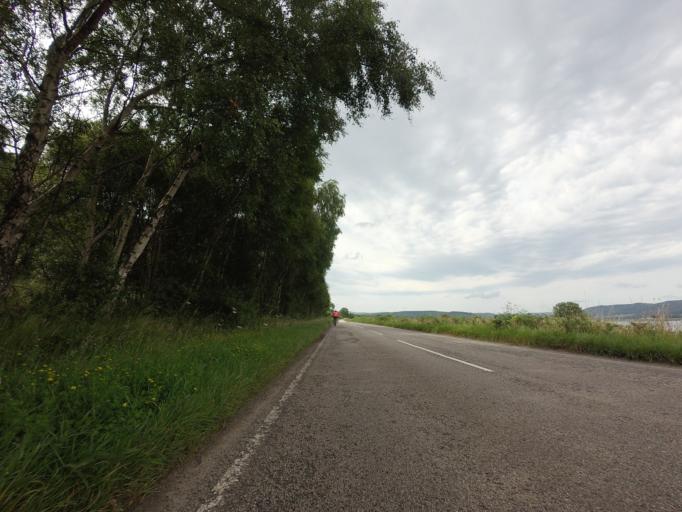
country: GB
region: Scotland
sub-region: Highland
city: Alness
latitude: 57.8693
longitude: -4.3410
